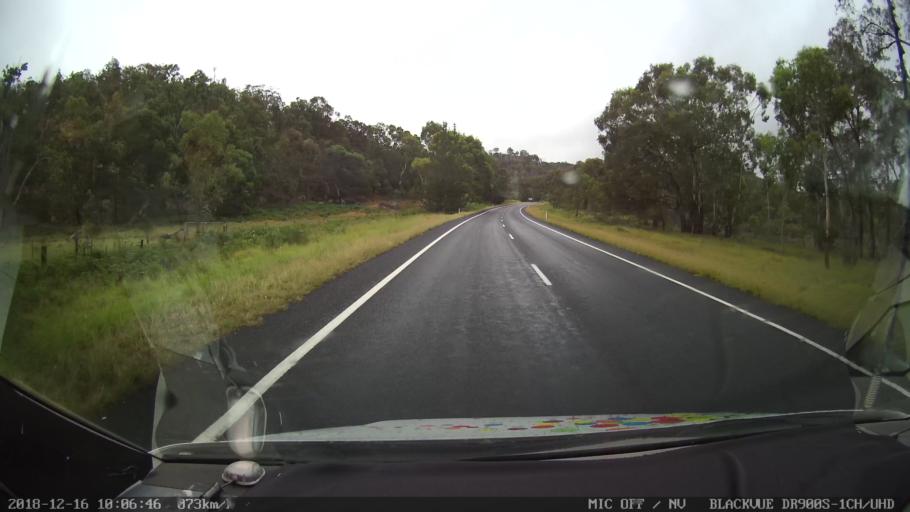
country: AU
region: New South Wales
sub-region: Glen Innes Severn
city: Glen Innes
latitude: -29.3418
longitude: 151.8924
